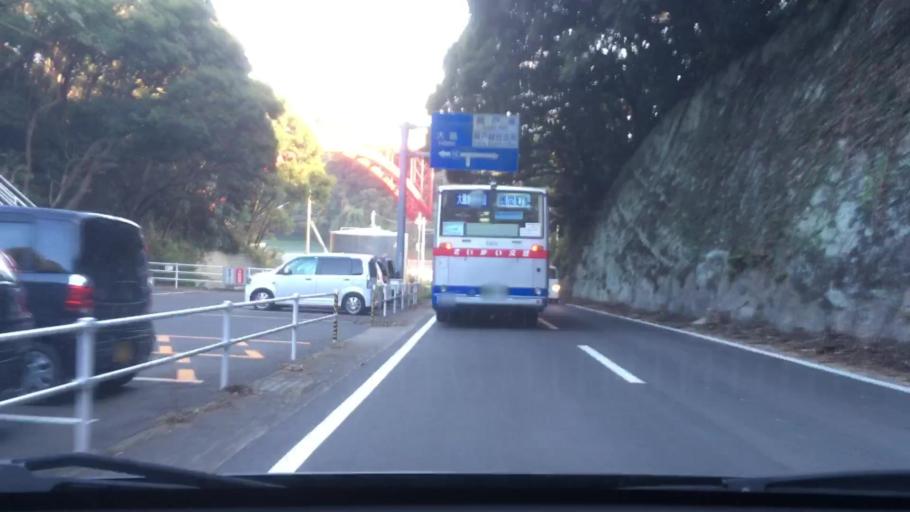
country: JP
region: Nagasaki
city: Sasebo
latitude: 33.0239
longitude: 129.5710
